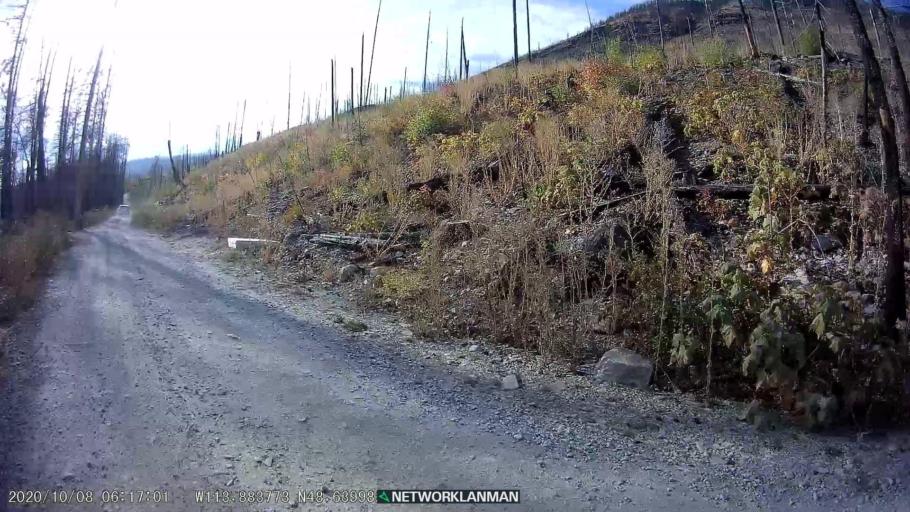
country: US
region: Montana
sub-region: Flathead County
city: Columbia Falls
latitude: 48.6400
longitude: -113.8839
